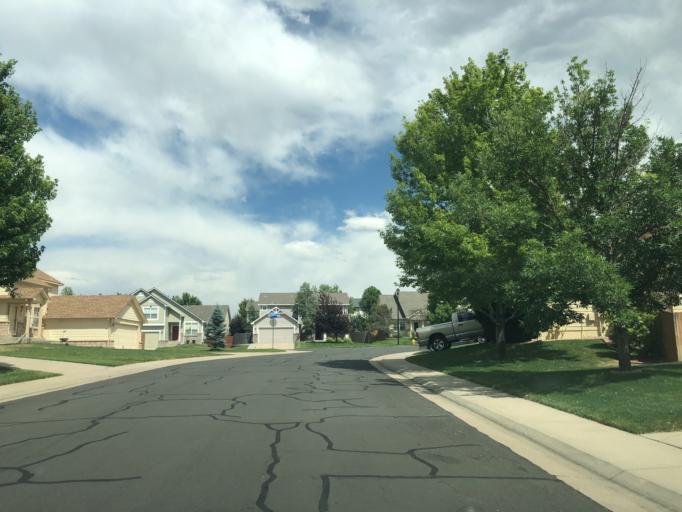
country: US
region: Colorado
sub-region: Arapahoe County
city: Dove Valley
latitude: 39.6201
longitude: -104.7702
